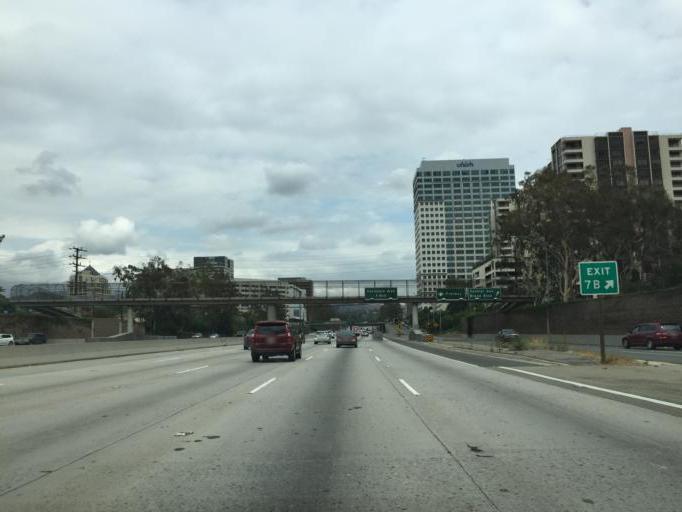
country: US
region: California
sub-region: Los Angeles County
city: North Glendale
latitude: 34.1562
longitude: -118.2631
